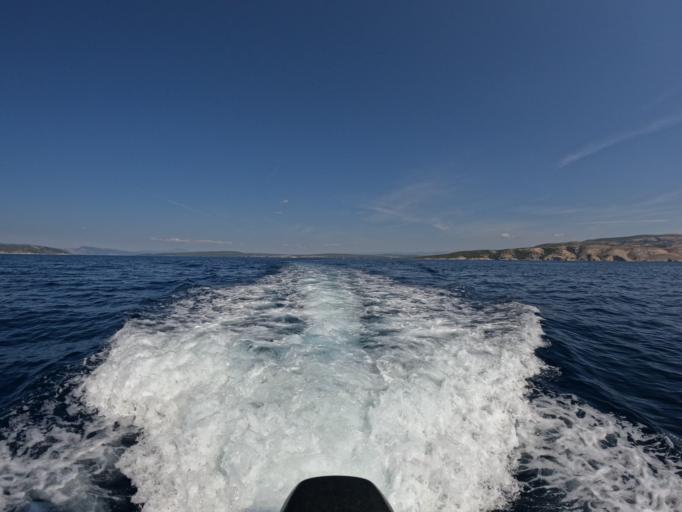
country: HR
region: Primorsko-Goranska
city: Punat
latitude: 44.9492
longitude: 14.6137
